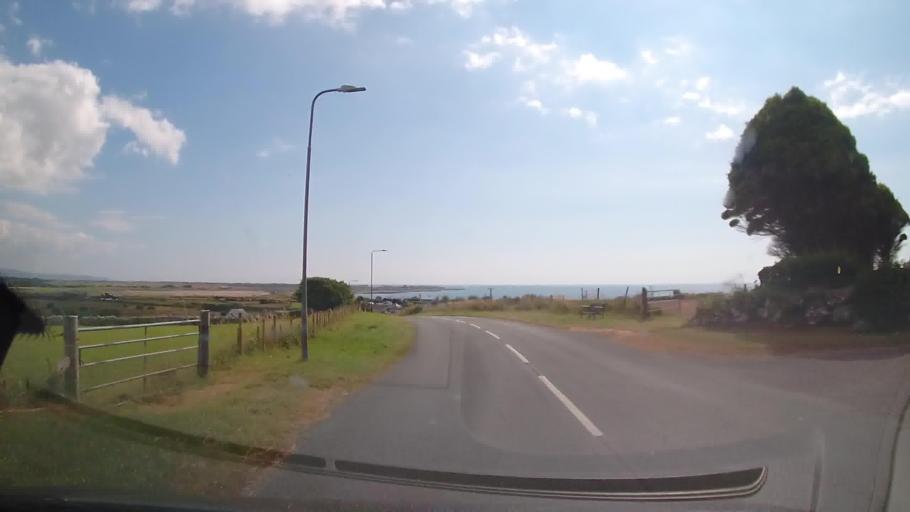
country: GB
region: Wales
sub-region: Gwynedd
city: Llanfair
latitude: 52.8409
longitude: -4.1201
